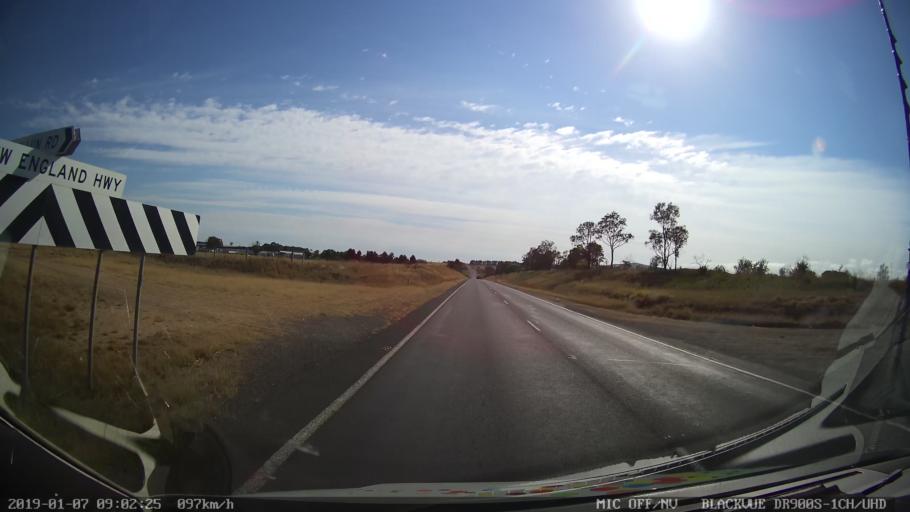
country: AU
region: New South Wales
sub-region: Armidale Dumaresq
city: Armidale
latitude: -30.7350
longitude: 151.4224
